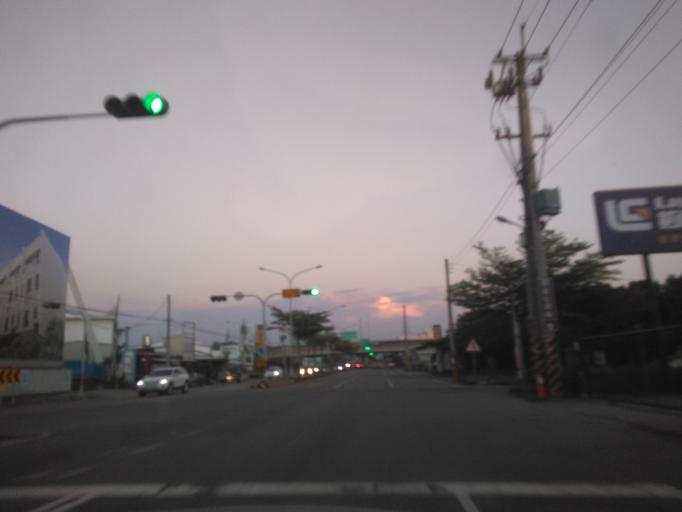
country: TW
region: Taiwan
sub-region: Changhua
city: Chang-hua
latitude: 24.0868
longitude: 120.5959
